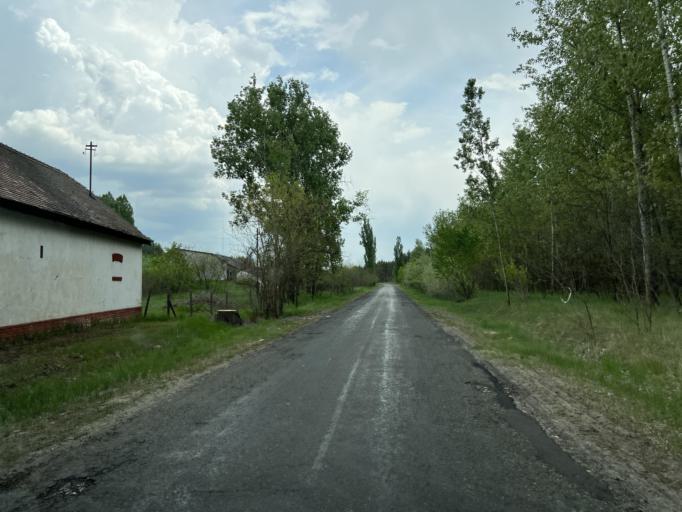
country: HU
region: Pest
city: Csemo
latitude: 47.1070
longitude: 19.7209
